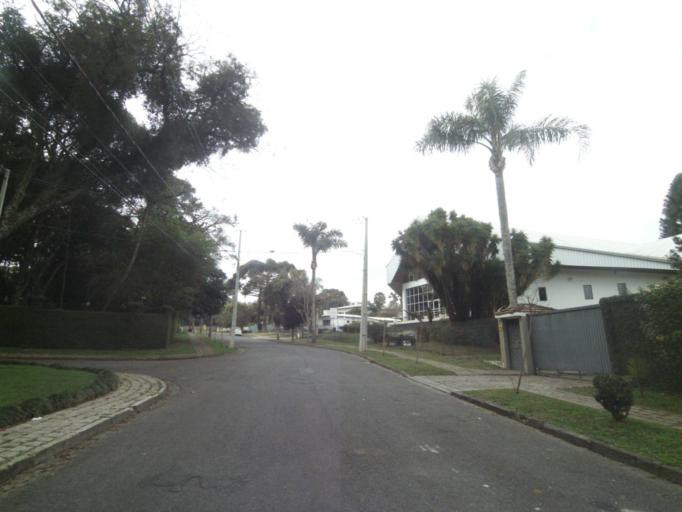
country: BR
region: Parana
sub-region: Curitiba
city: Curitiba
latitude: -25.4461
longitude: -49.2999
